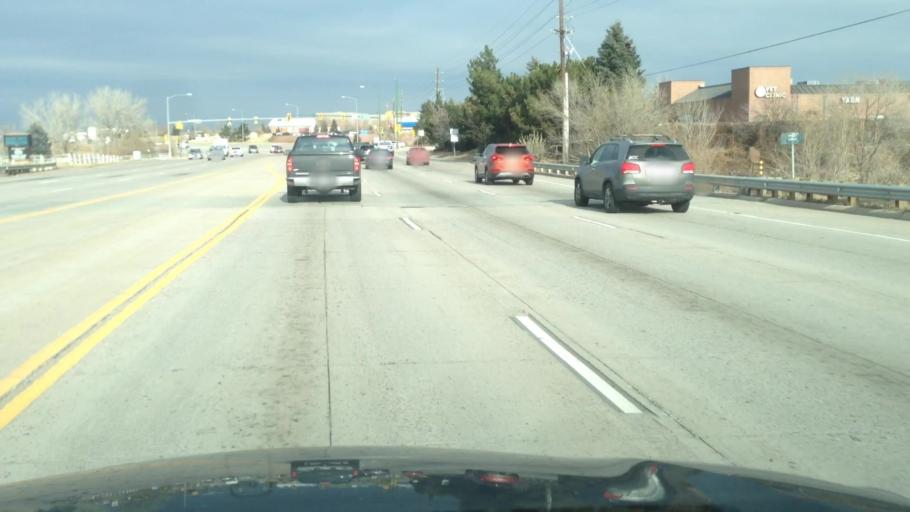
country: US
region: Colorado
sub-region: Arapahoe County
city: Dove Valley
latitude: 39.6089
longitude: -104.8096
